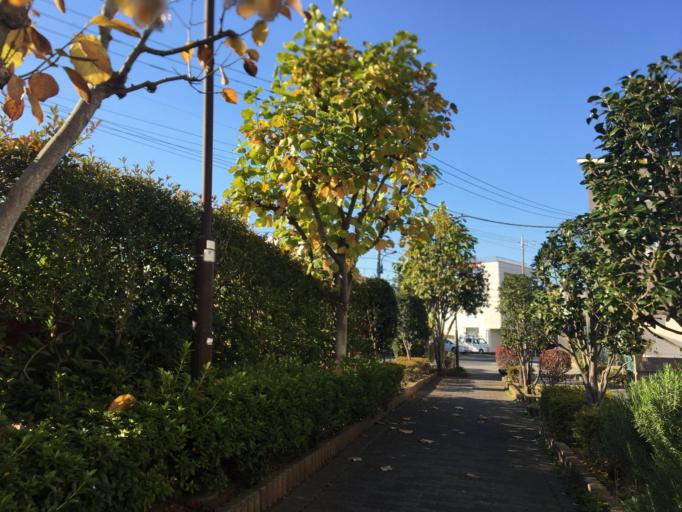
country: JP
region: Tokyo
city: Urayasu
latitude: 35.7174
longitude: 139.8921
